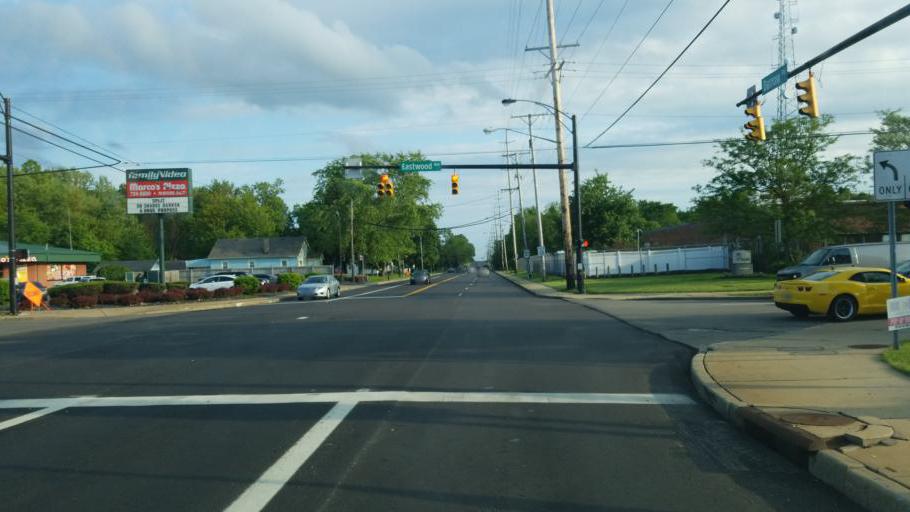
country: US
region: Ohio
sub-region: Summit County
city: Tallmadge
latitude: 41.0845
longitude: -81.4417
